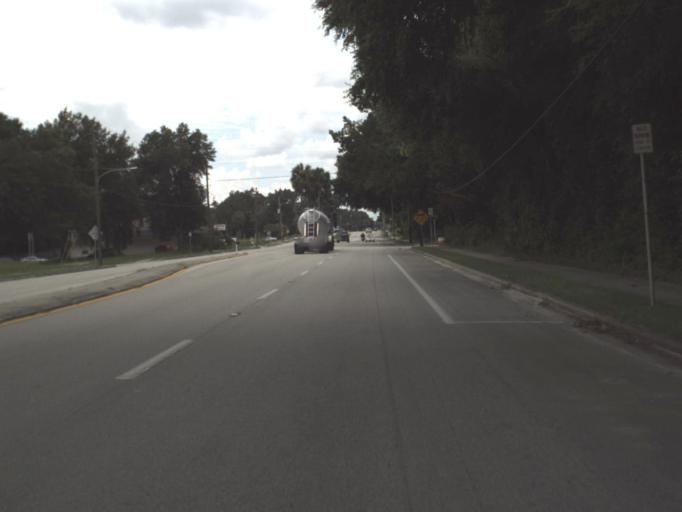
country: US
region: Florida
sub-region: Alachua County
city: Newberry
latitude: 29.6521
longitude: -82.6068
